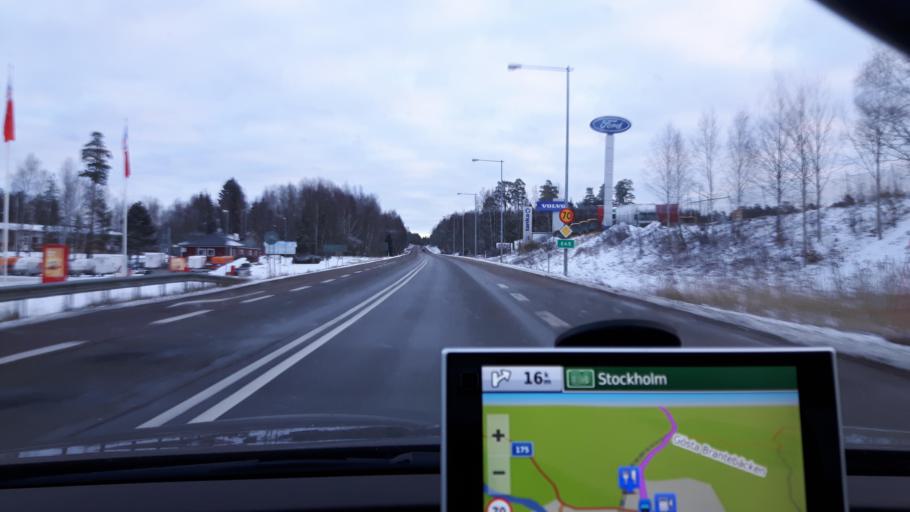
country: SE
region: Vaermland
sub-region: Saffle Kommun
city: Saeffle
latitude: 59.1413
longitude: 12.9413
